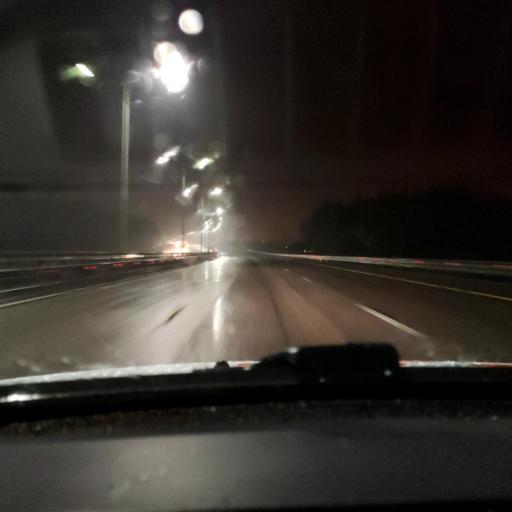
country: RU
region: Voronezj
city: Somovo
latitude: 51.7284
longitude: 39.3114
